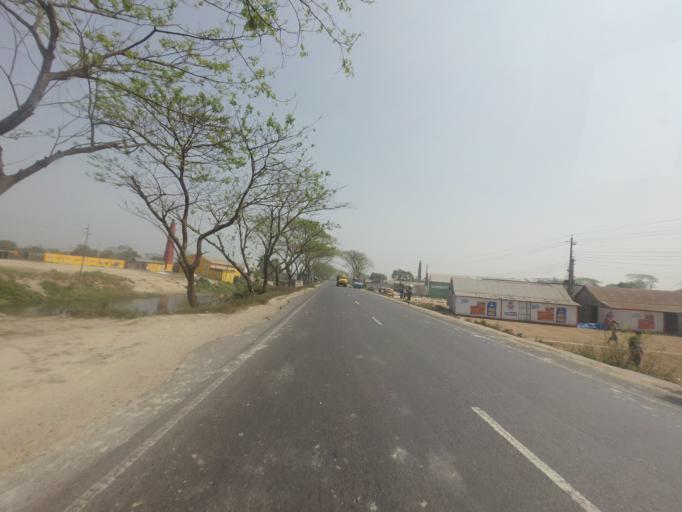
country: BD
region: Dhaka
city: Bhairab Bazar
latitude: 24.0440
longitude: 91.0612
